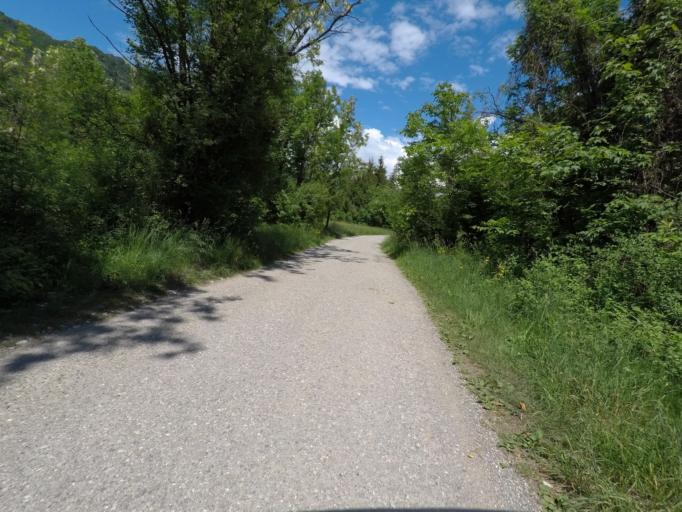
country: IT
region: Friuli Venezia Giulia
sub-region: Provincia di Udine
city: Chiaulis
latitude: 46.4034
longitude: 12.9983
